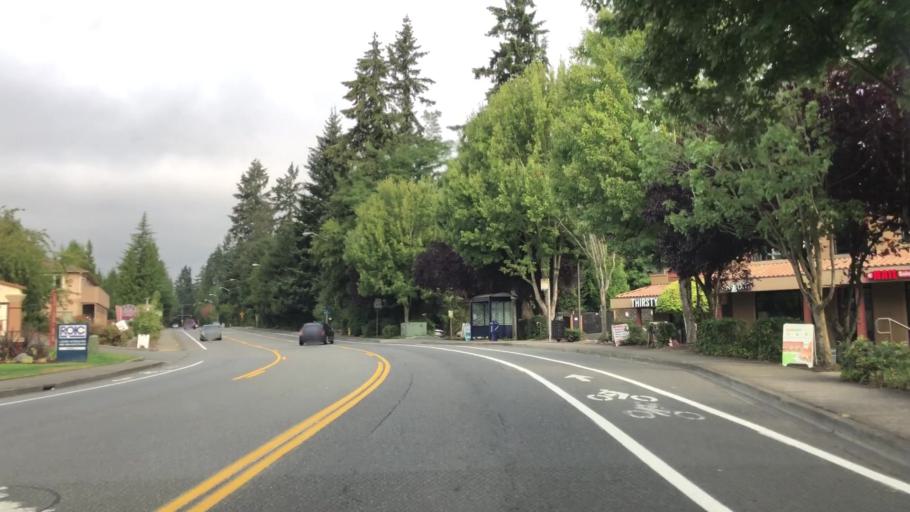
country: US
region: Washington
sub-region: King County
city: Redmond
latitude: 47.6668
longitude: -122.1646
